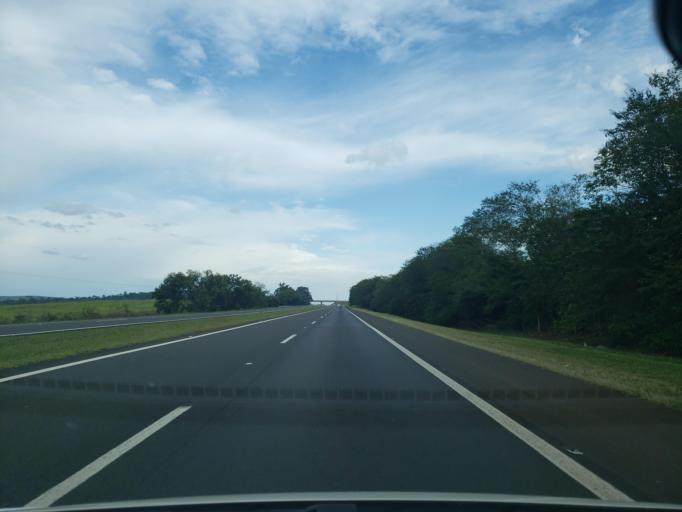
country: BR
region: Sao Paulo
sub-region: Itirapina
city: Itirapina
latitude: -22.2669
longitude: -47.9267
